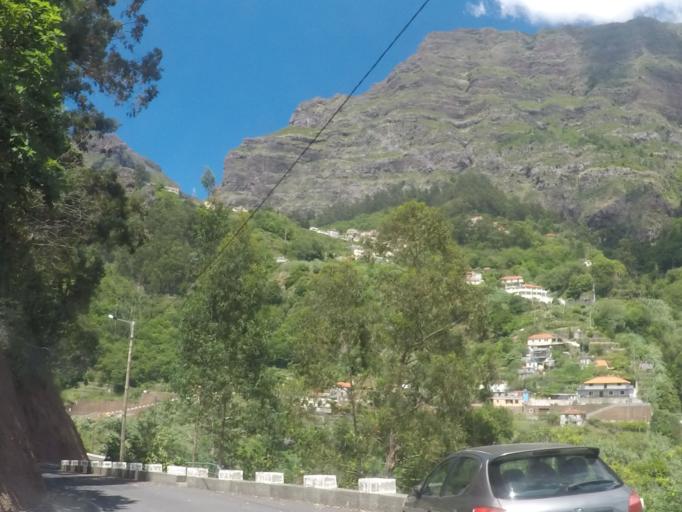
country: PT
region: Madeira
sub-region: Camara de Lobos
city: Curral das Freiras
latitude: 32.7163
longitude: -16.9705
